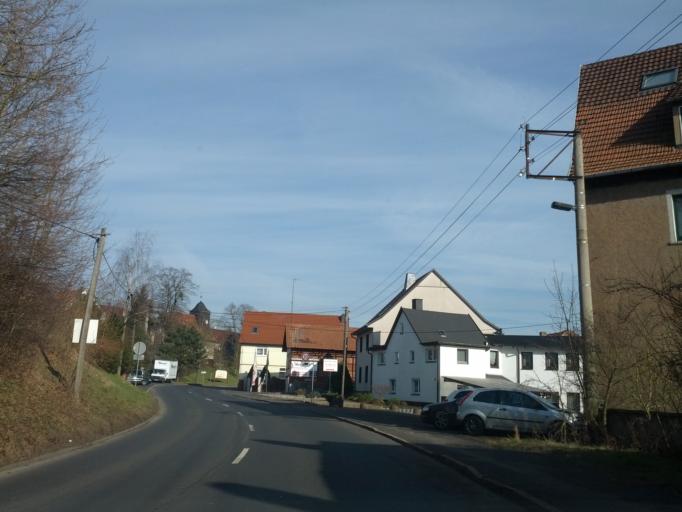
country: DE
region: Thuringia
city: Bischofroda
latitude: 50.9891
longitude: 10.3763
